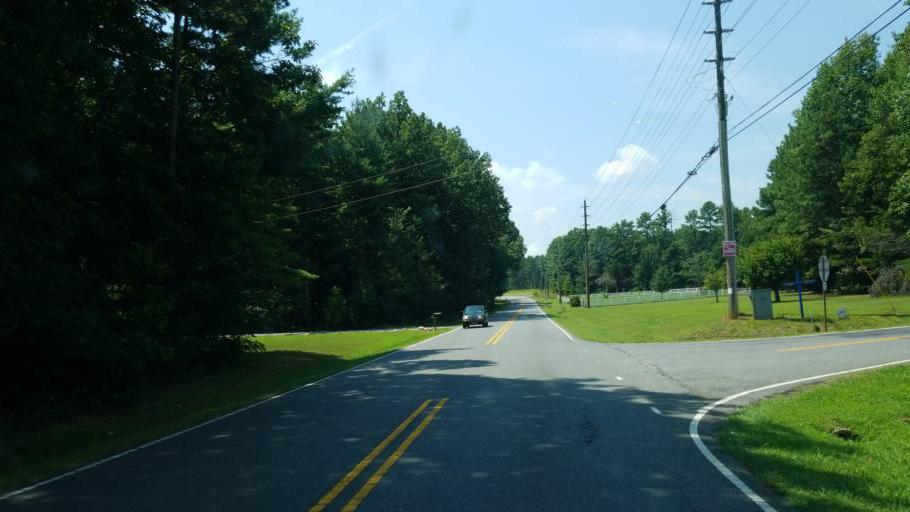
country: US
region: North Carolina
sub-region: Gaston County
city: Tryon
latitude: 35.3183
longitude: -81.3658
